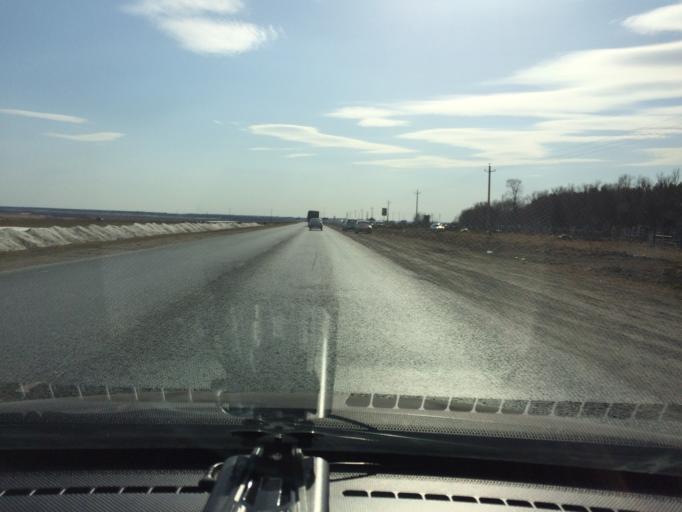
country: RU
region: Mariy-El
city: Yoshkar-Ola
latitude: 56.6999
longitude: 48.0666
